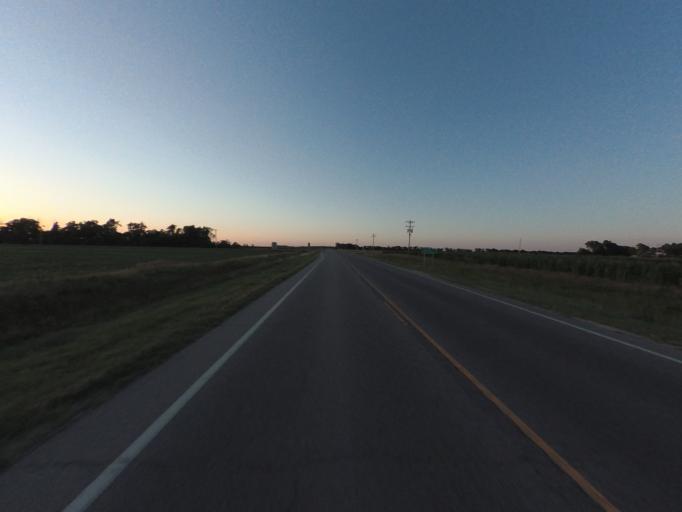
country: US
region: Kansas
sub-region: Rice County
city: Sterling
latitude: 38.2455
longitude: -98.2067
